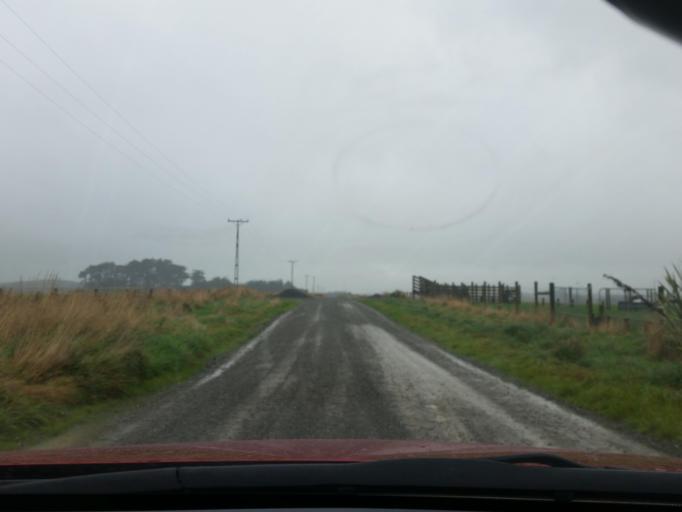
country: NZ
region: Southland
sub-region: Invercargill City
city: Invercargill
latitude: -46.3473
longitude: 168.3721
